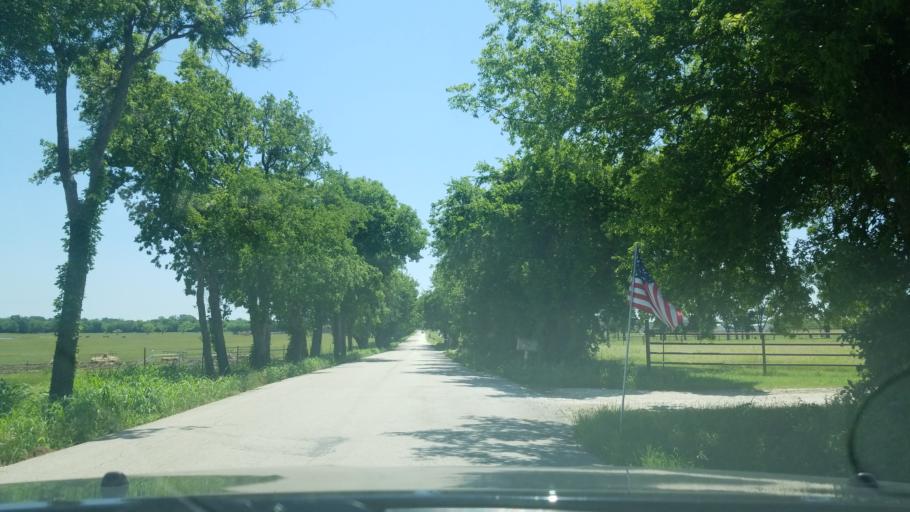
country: US
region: Texas
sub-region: Denton County
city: Sanger
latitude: 33.3420
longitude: -97.2315
